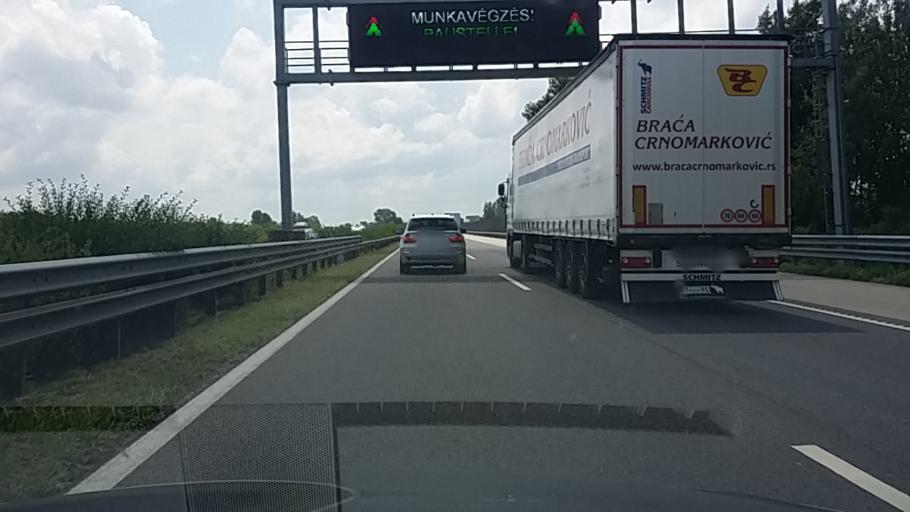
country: HU
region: Pest
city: Ujhartyan
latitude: 47.2267
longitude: 19.3996
